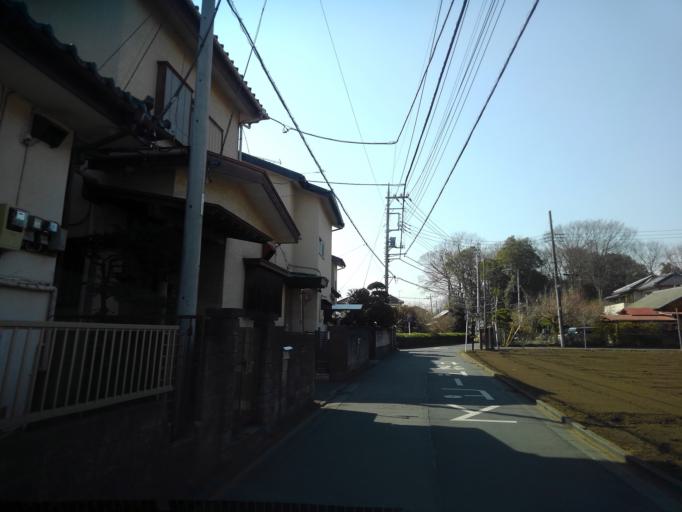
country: JP
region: Saitama
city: Tokorozawa
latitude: 35.7951
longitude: 139.4886
